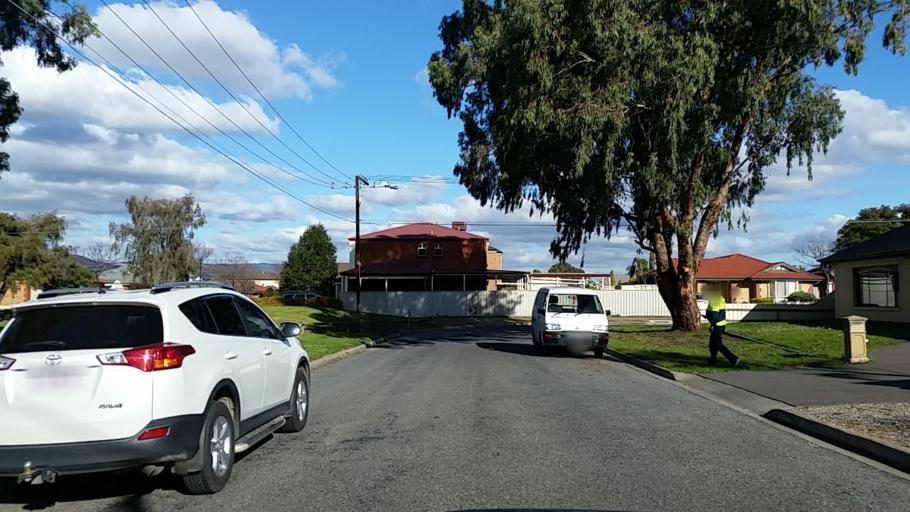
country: AU
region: South Australia
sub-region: Campbelltown
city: Paradise
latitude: -34.8540
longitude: 138.6696
